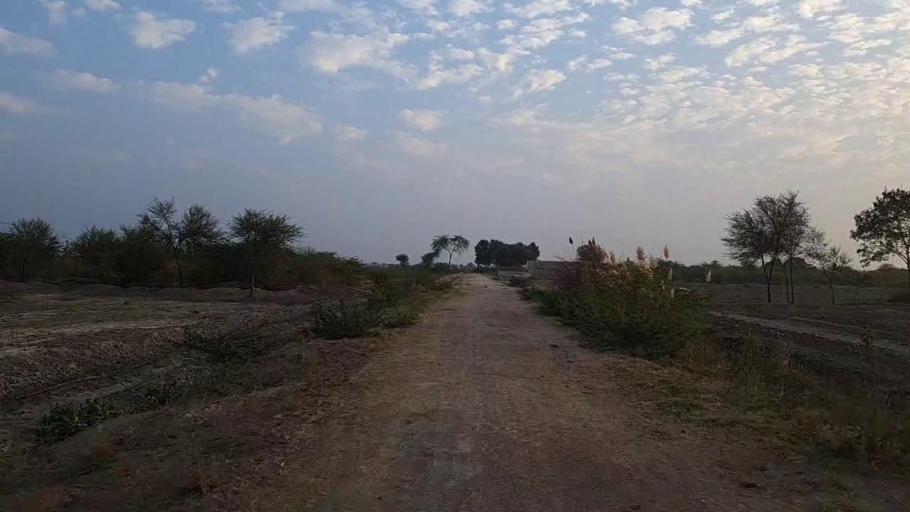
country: PK
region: Sindh
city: Pithoro
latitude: 25.4421
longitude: 69.3380
